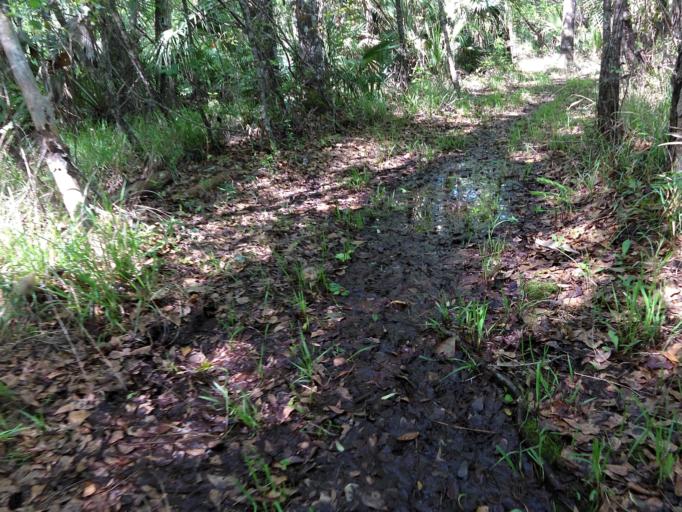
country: US
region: Florida
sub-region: Putnam County
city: Palatka
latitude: 29.6846
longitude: -81.7439
